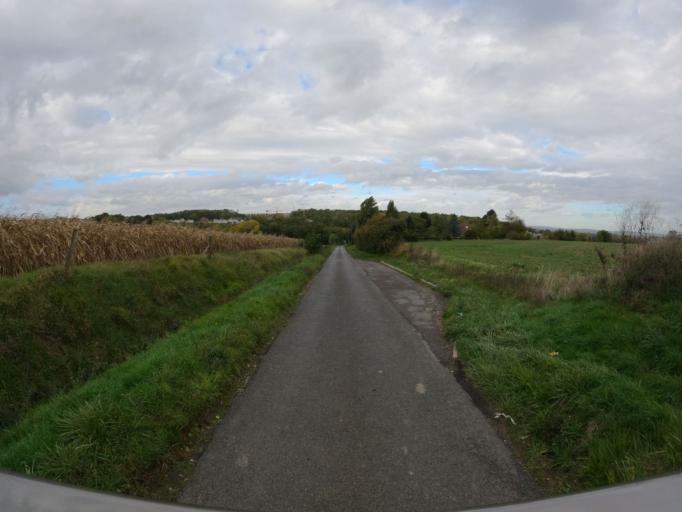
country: FR
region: Ile-de-France
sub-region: Departement de Seine-et-Marne
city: Montry
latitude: 48.8740
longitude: 2.8286
